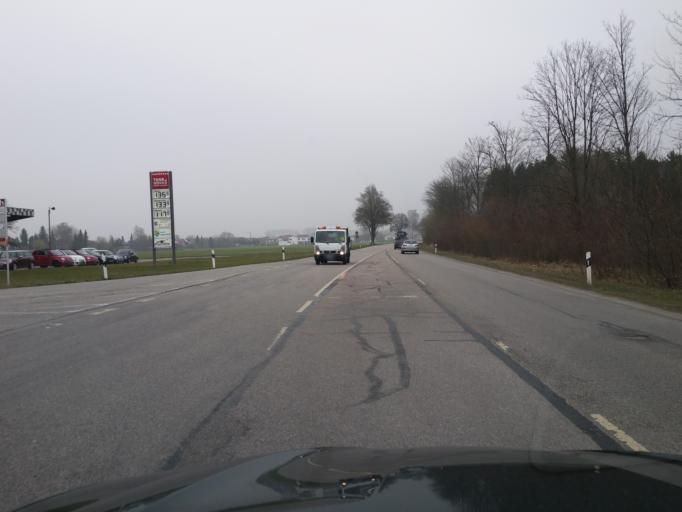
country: DE
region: Bavaria
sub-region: Lower Bavaria
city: Stallwang
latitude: 48.5643
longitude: 12.2067
